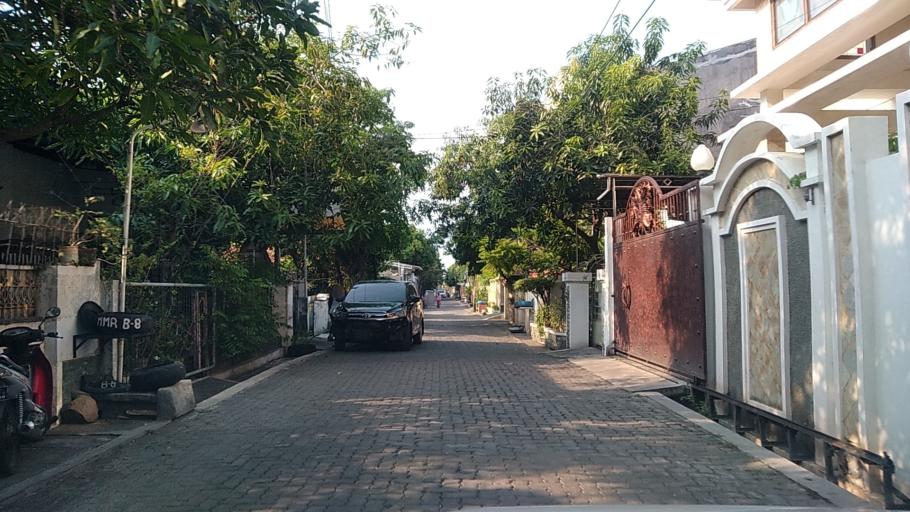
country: ID
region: Central Java
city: Semarang
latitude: -6.9565
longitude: 110.4073
